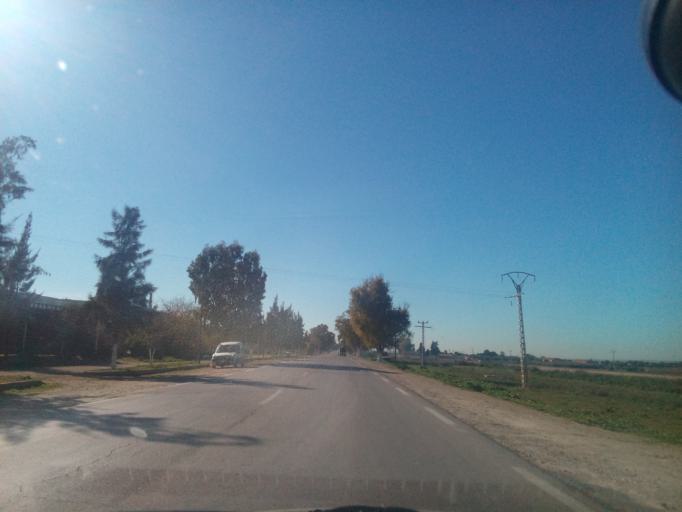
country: DZ
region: Chlef
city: Boukadir
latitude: 36.0142
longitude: 1.0277
